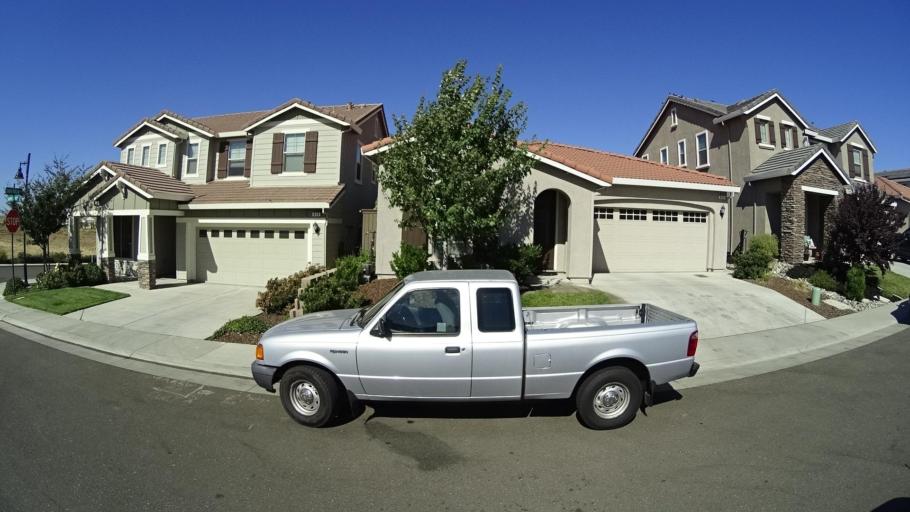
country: US
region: California
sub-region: Placer County
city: Rocklin
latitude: 38.8349
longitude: -121.2703
